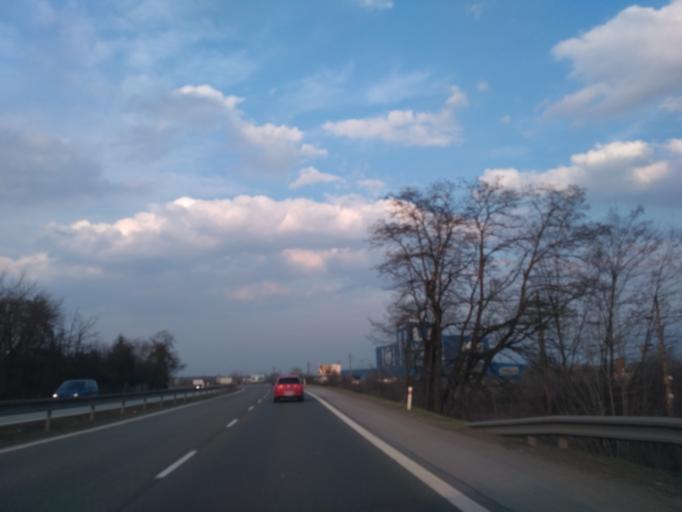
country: SK
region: Kosicky
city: Kosice
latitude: 48.6306
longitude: 21.1901
